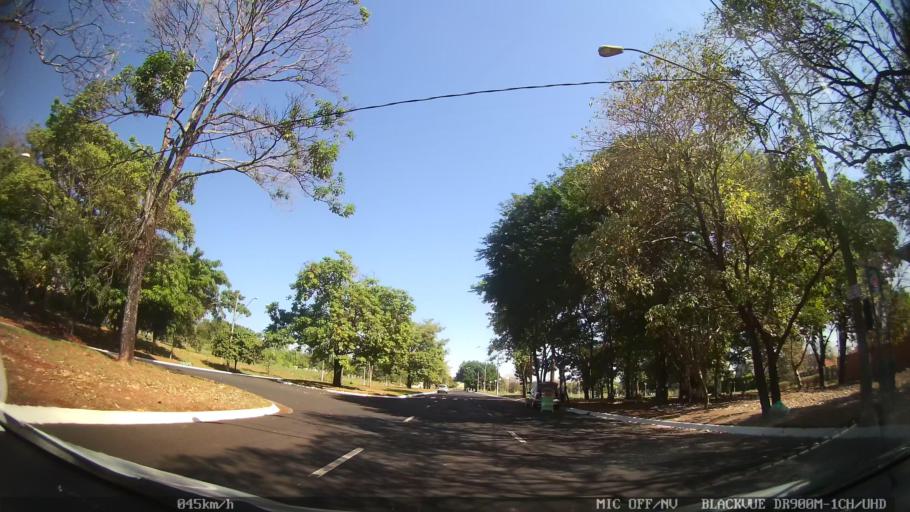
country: BR
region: Sao Paulo
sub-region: Ribeirao Preto
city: Ribeirao Preto
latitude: -21.2159
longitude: -47.7843
